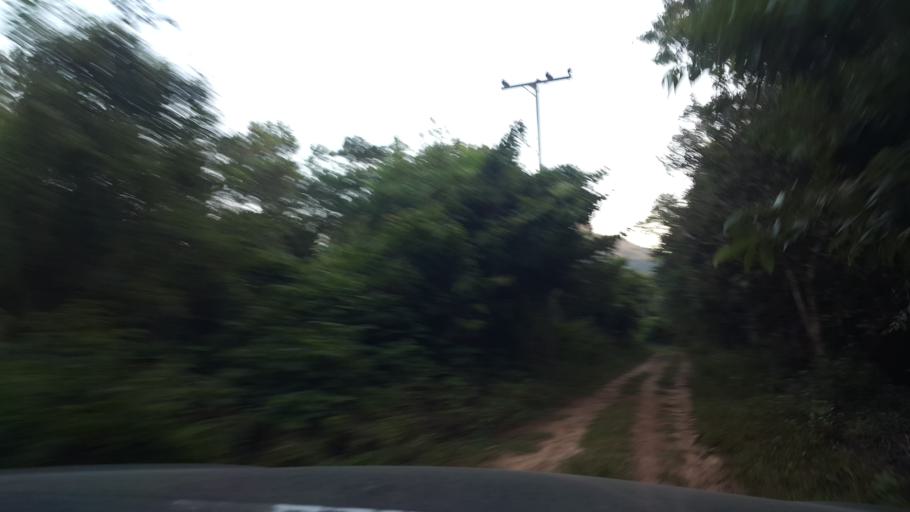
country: TH
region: Chiang Mai
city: San Kamphaeng
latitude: 18.6904
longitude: 99.2014
